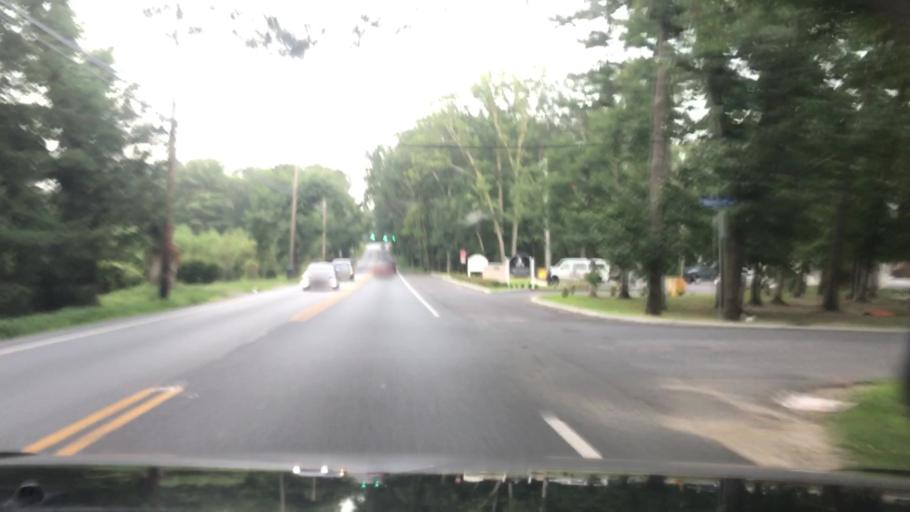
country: US
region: New Jersey
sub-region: Ocean County
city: Lakewood
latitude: 40.0753
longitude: -74.2498
